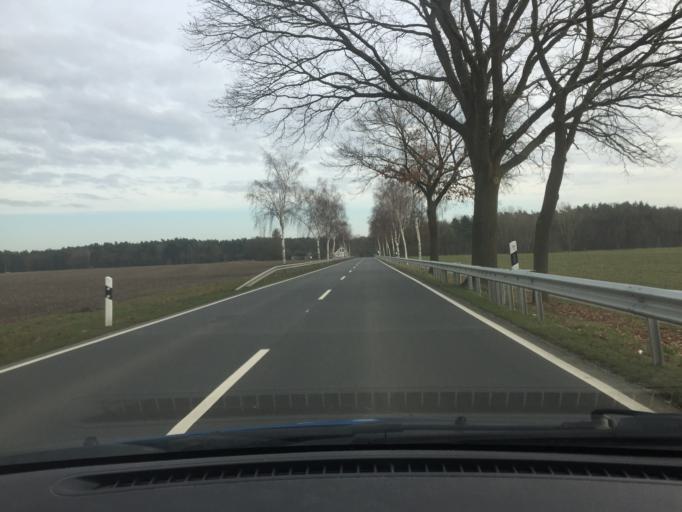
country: DE
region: Lower Saxony
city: Waddeweitz
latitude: 52.9843
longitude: 11.0060
